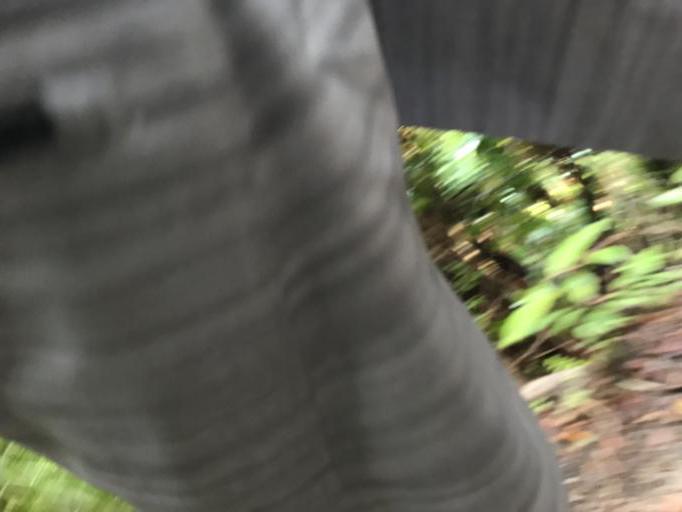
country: NZ
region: Marlborough
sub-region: Marlborough District
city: Picton
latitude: -41.2635
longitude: 173.9261
